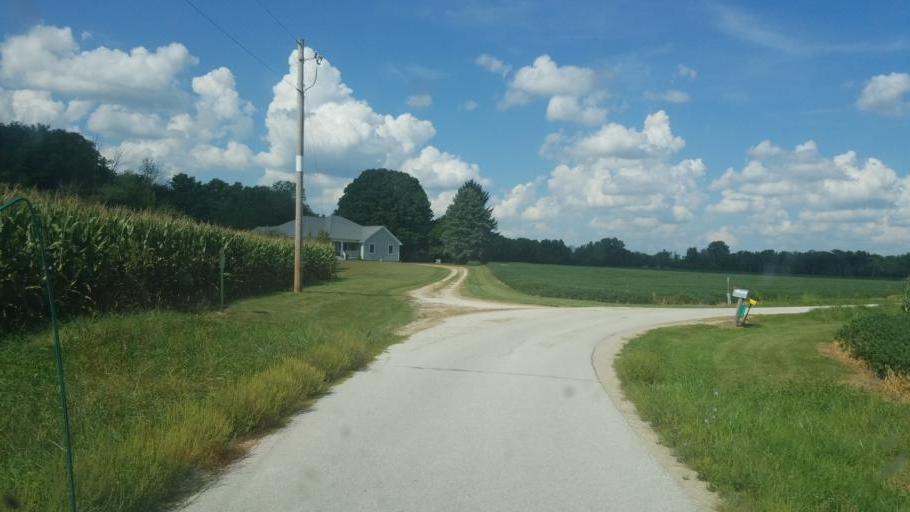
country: US
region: Ohio
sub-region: Wyandot County
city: Carey
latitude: 40.9720
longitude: -83.2423
